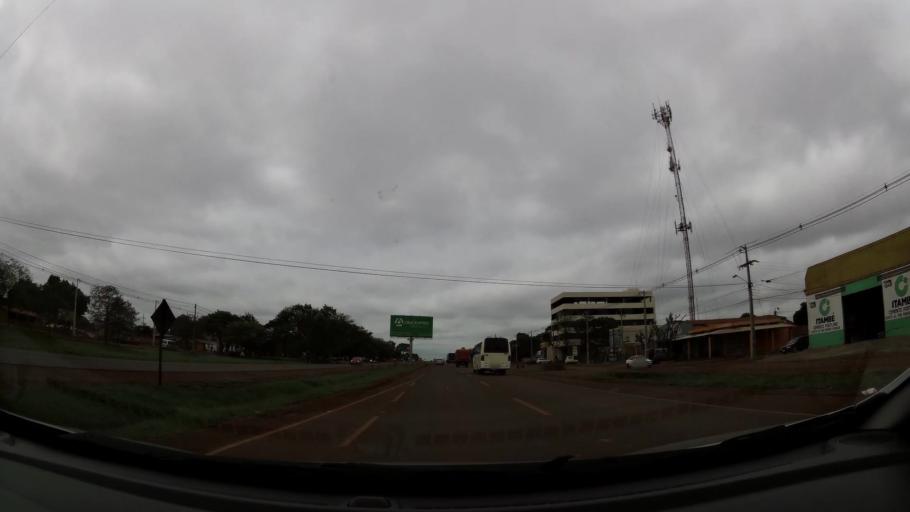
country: PY
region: Alto Parana
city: Ciudad del Este
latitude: -25.4920
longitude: -54.7381
